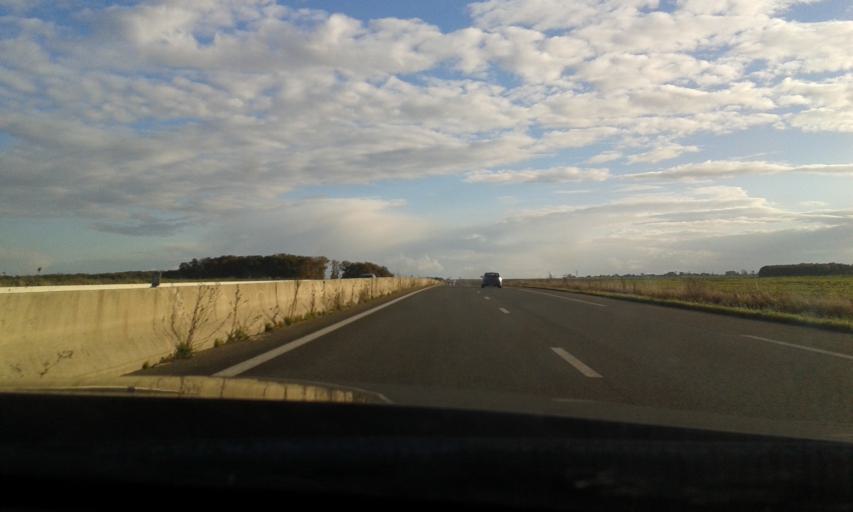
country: FR
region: Centre
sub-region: Departement d'Eure-et-Loir
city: Bailleau-l'Eveque
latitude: 48.5777
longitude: 1.4321
